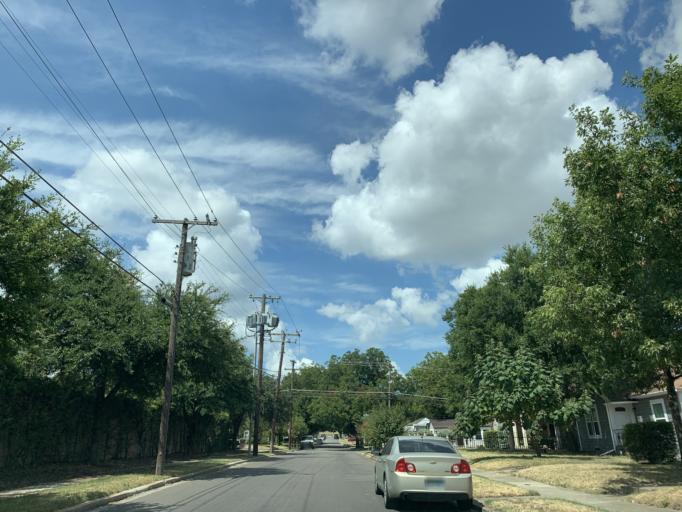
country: US
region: Texas
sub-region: Dallas County
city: Cockrell Hill
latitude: 32.7432
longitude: -96.8582
